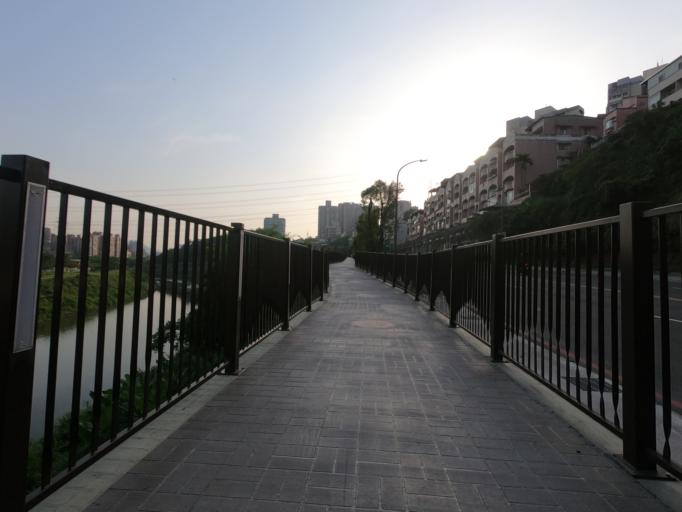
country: TW
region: Taiwan
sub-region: Keelung
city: Keelung
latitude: 25.0757
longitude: 121.6439
